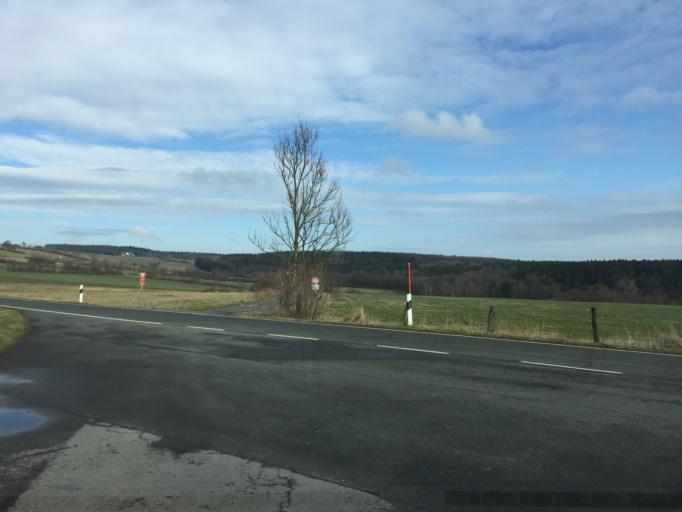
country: DE
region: Lower Saxony
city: Aerzen
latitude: 52.0973
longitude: 9.1627
